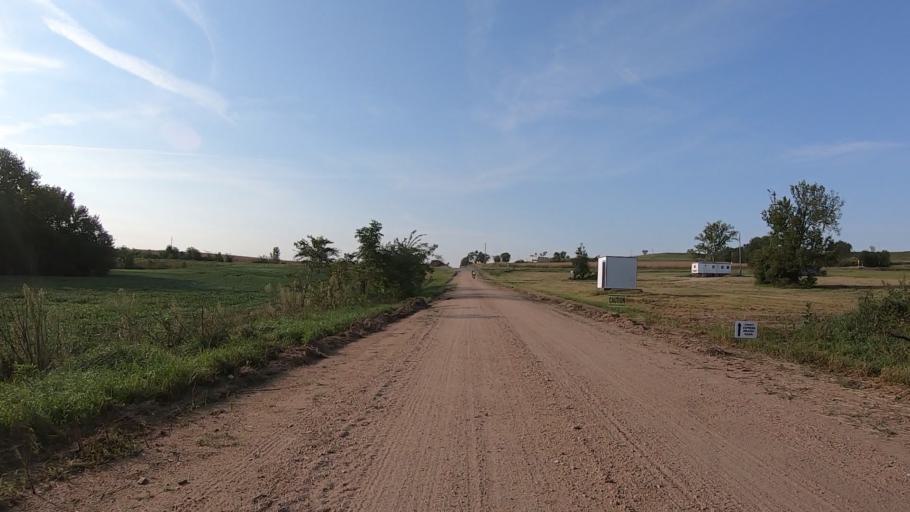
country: US
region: Kansas
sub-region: Marshall County
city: Blue Rapids
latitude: 39.6911
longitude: -96.7792
